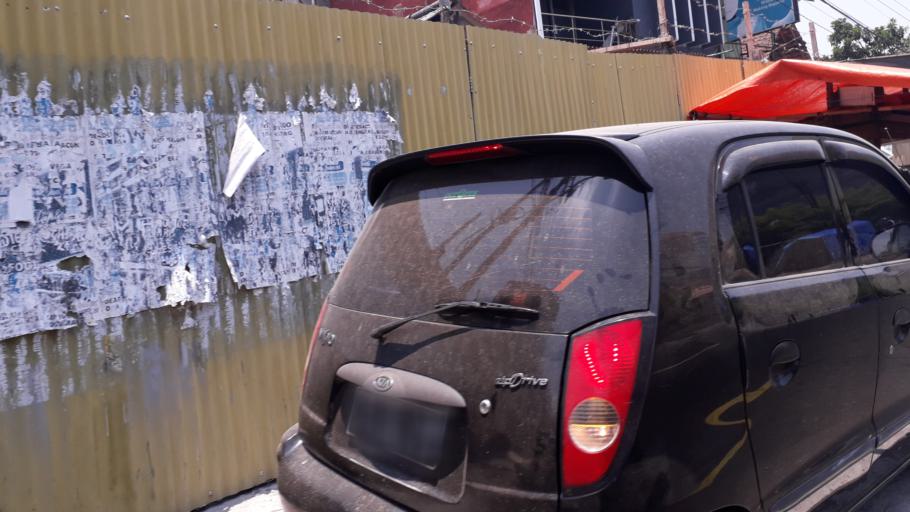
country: ID
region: Daerah Istimewa Yogyakarta
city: Yogyakarta
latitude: -7.7650
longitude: 110.3691
